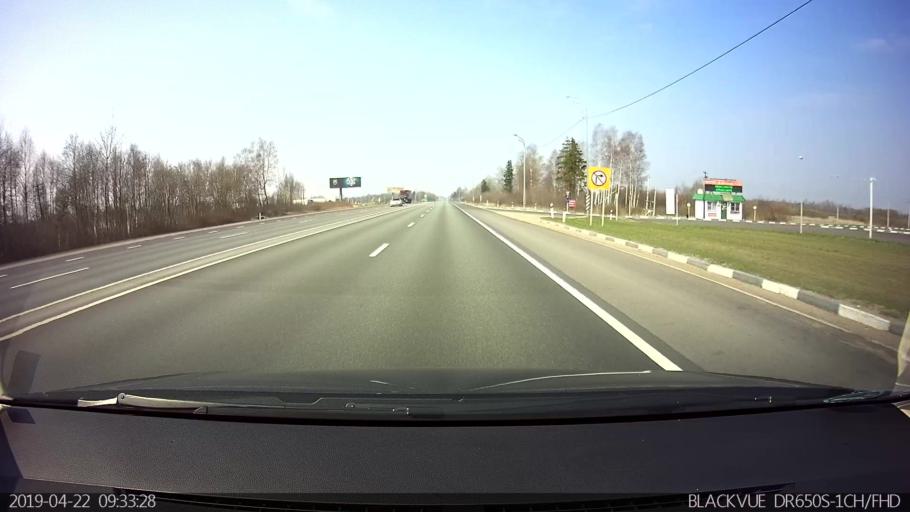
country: RU
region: Smolensk
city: Rudnya
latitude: 54.6957
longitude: 31.1217
